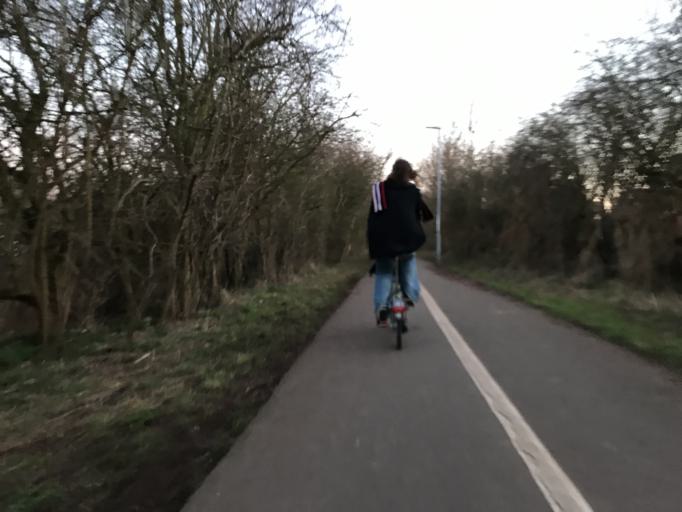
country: GB
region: England
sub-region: Lincolnshire
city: Holton le Clay
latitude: 53.5271
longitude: -0.0650
